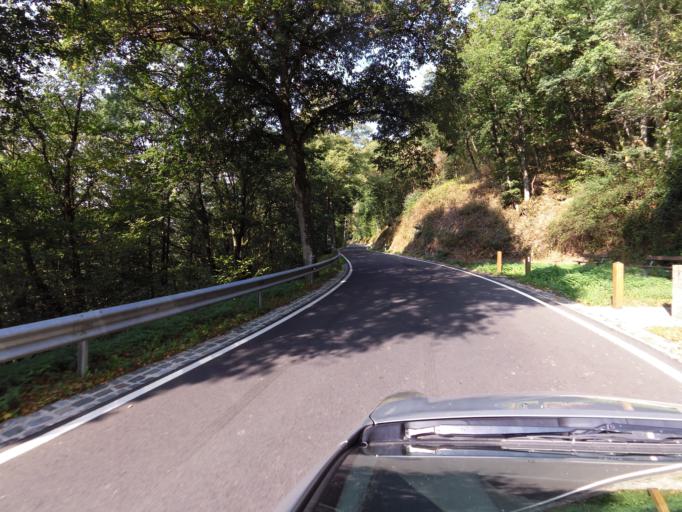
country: LU
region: Diekirch
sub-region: Canton de Wiltz
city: Goesdorf
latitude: 49.9150
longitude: 5.9923
